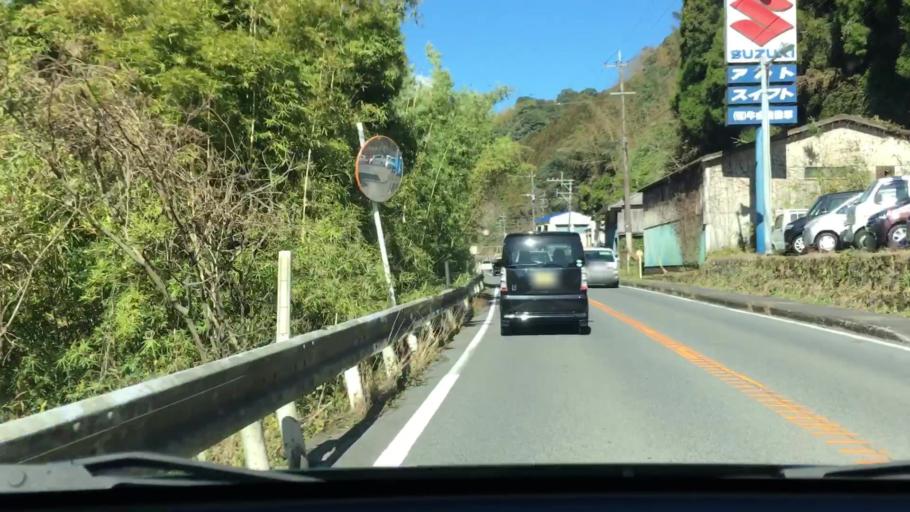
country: JP
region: Kagoshima
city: Kagoshima-shi
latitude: 31.6459
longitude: 130.5142
